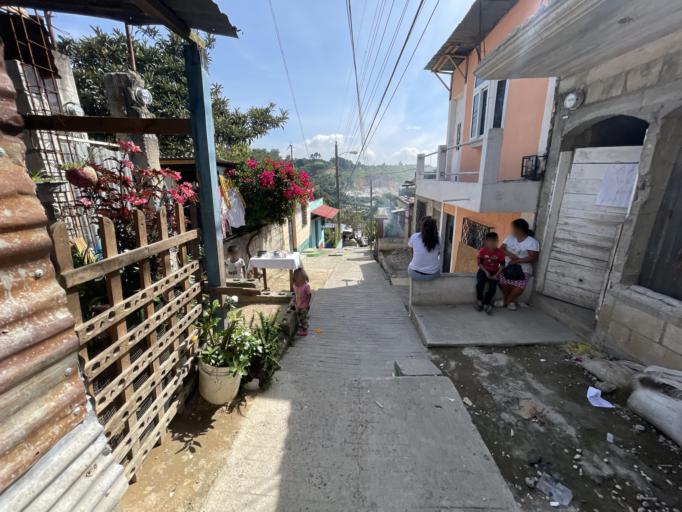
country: GT
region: Guatemala
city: Mixco
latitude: 14.6816
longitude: -90.5748
